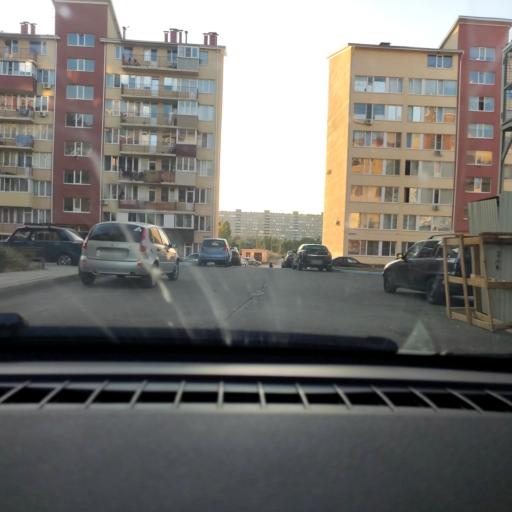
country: RU
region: Voronezj
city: Novaya Usman'
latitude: 51.6072
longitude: 39.3873
